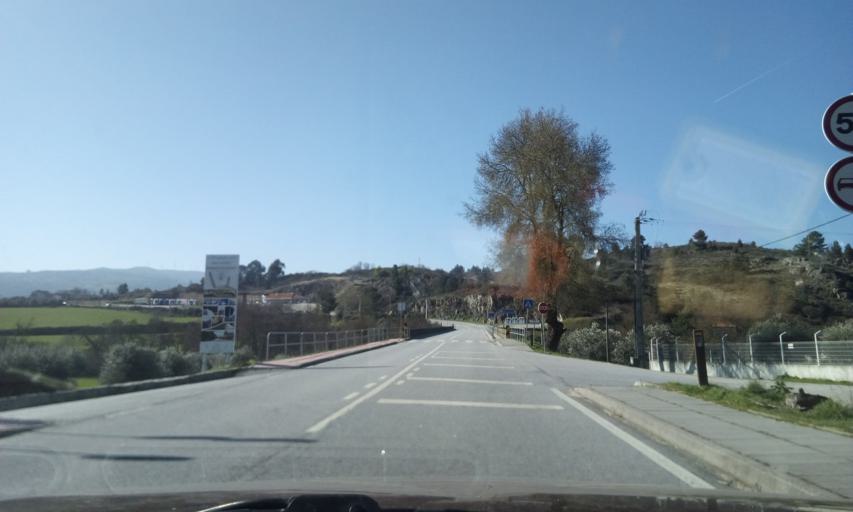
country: PT
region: Guarda
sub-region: Celorico da Beira
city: Celorico da Beira
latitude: 40.6548
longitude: -7.3824
